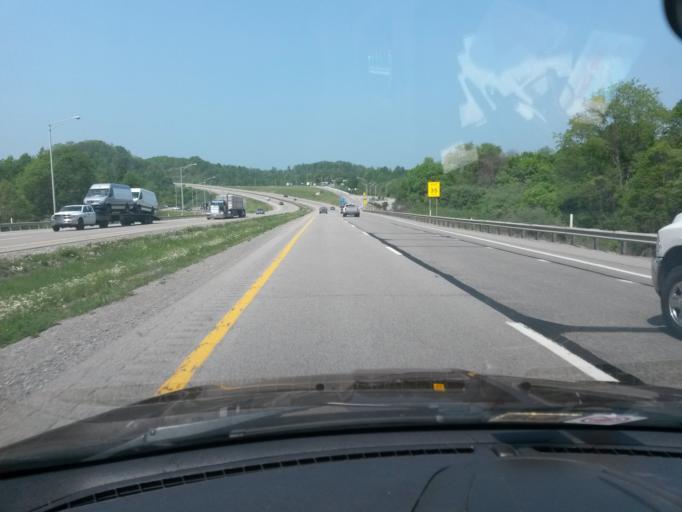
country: US
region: West Virginia
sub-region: Lewis County
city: Weston
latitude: 38.9127
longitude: -80.5882
